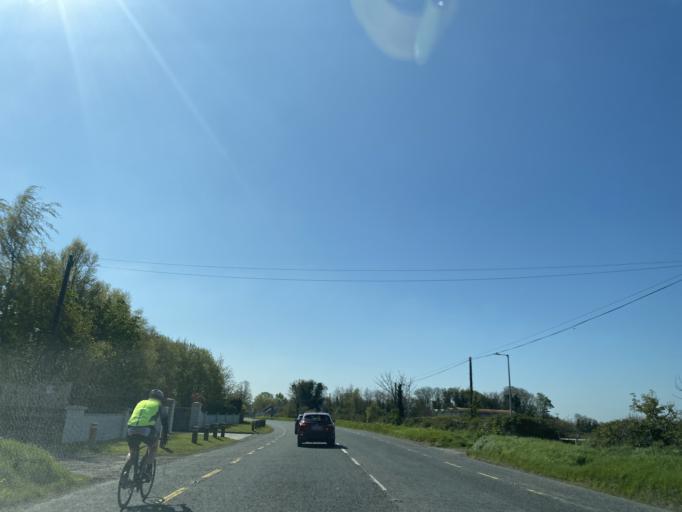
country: IE
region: Leinster
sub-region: Kildare
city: Maynooth
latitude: 53.3265
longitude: -6.6080
